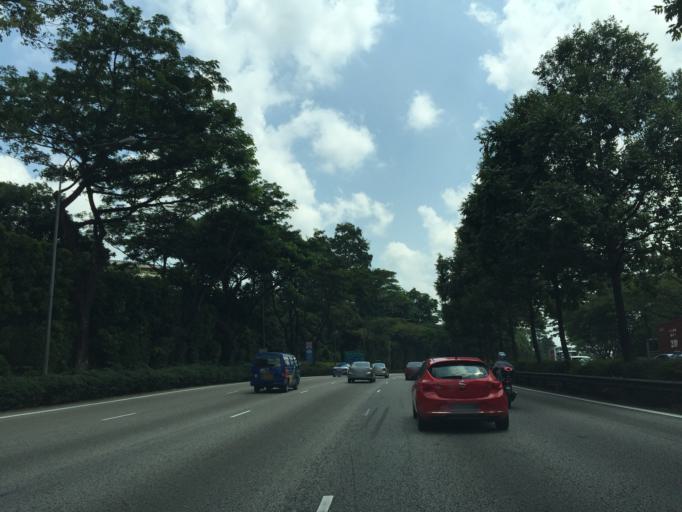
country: SG
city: Singapore
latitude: 1.3338
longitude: 103.8131
